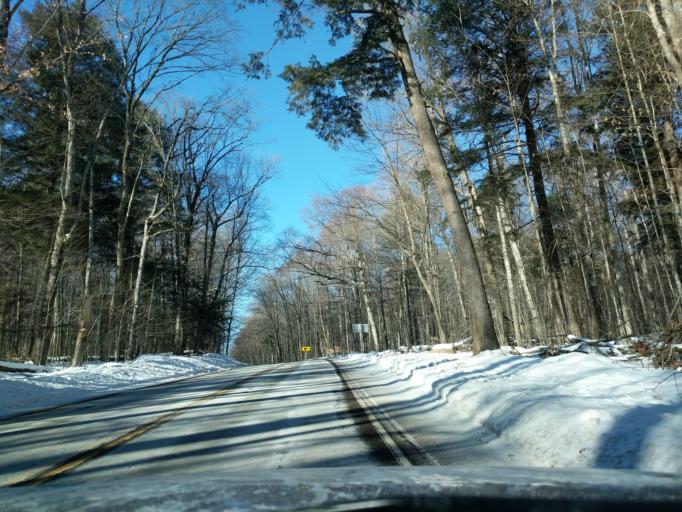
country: US
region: Wisconsin
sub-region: Menominee County
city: Keshena
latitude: 45.0893
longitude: -88.6271
